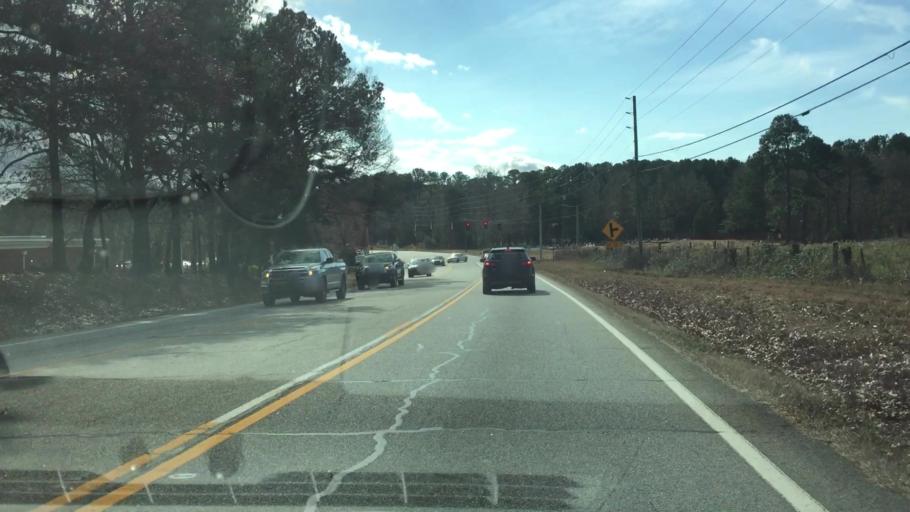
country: US
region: Georgia
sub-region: Henry County
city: McDonough
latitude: 33.5008
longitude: -84.1446
